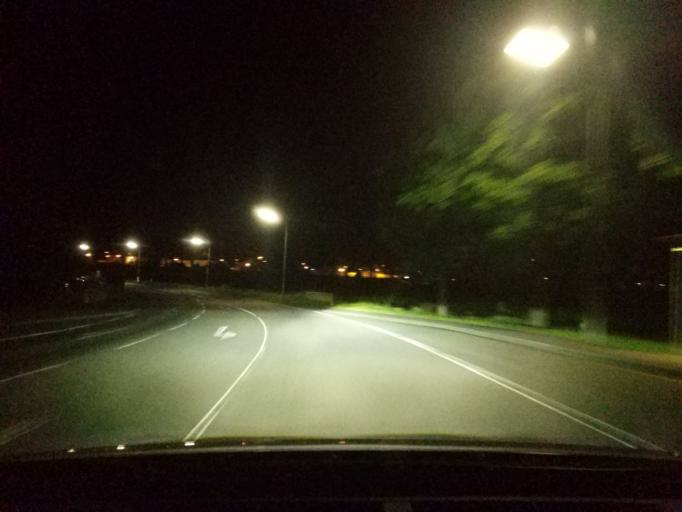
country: DE
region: Rheinland-Pfalz
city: Otterbach
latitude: 49.4833
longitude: 7.7235
